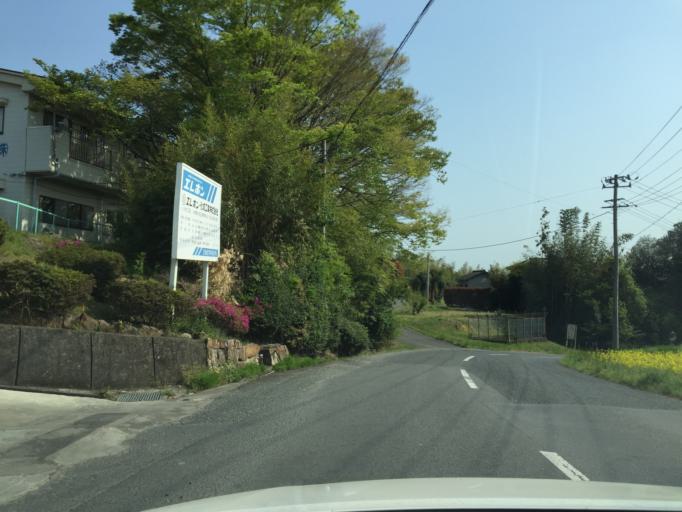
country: JP
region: Fukushima
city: Iwaki
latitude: 37.1294
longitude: 140.8697
